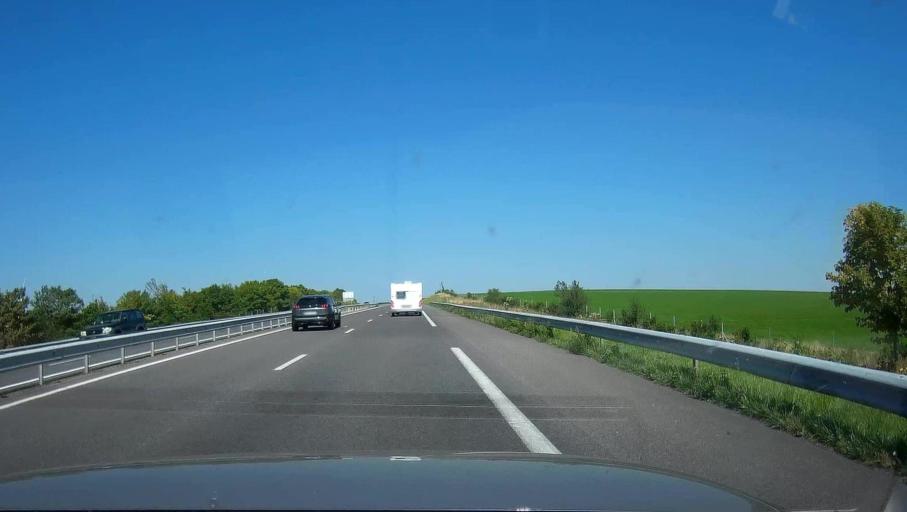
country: FR
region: Champagne-Ardenne
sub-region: Departement de l'Aube
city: Mailly-le-Camp
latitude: 48.6477
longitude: 4.1769
